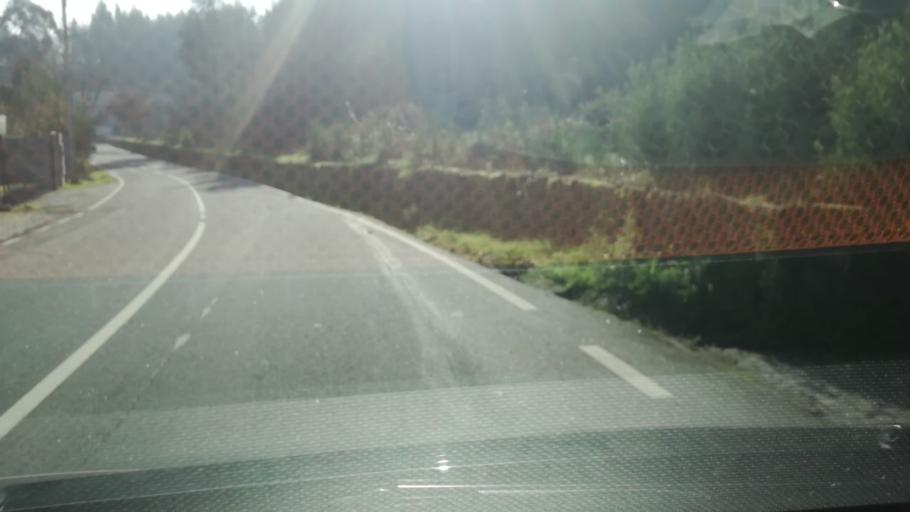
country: PT
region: Braga
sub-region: Guimaraes
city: Ponte
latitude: 41.5181
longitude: -8.3339
